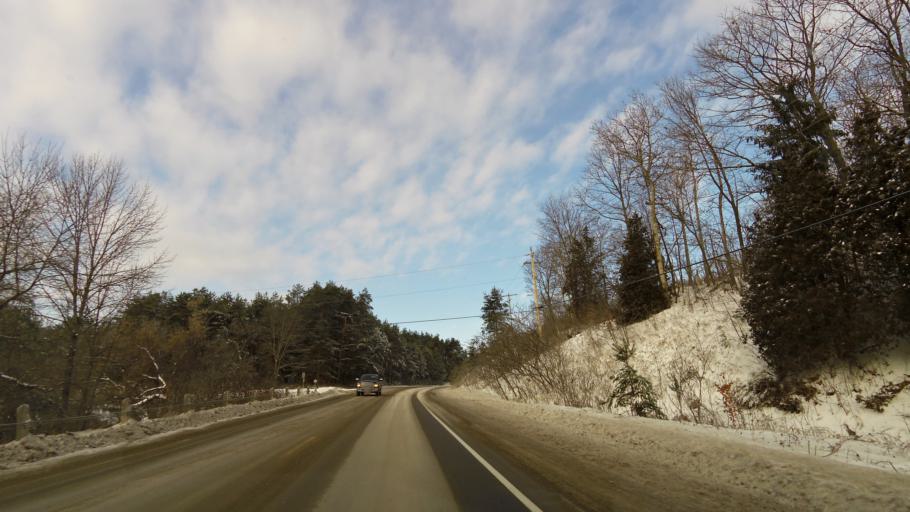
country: CA
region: Ontario
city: Quinte West
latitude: 44.1097
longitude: -77.7773
